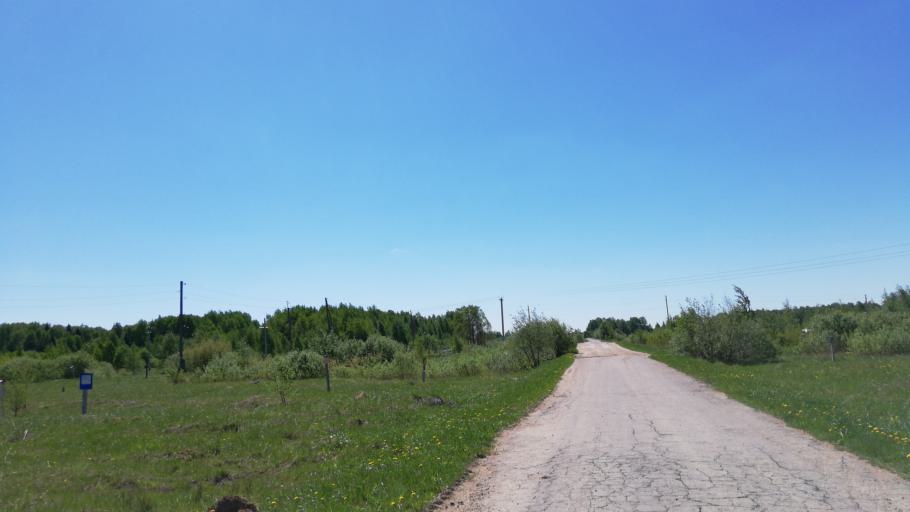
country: RU
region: Ivanovo
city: Pistsovo
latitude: 57.1259
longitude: 40.6013
